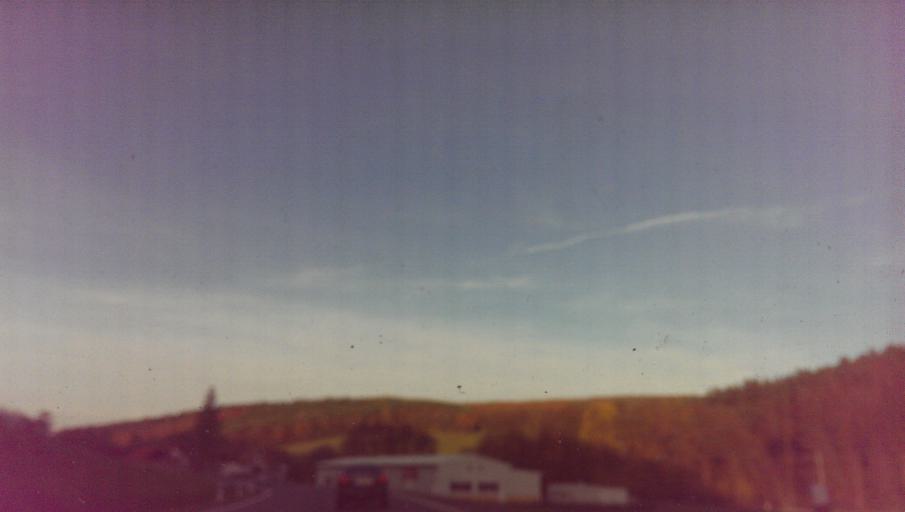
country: CZ
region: Zlin
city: Brezolupy
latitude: 49.1384
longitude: 17.6042
